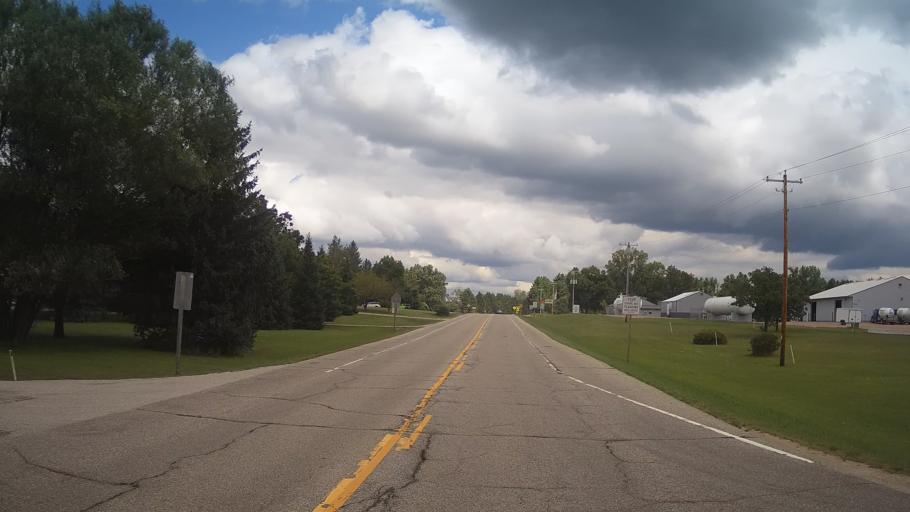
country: US
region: Wisconsin
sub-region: Marquette County
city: Westfield
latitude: 44.0363
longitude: -89.5160
